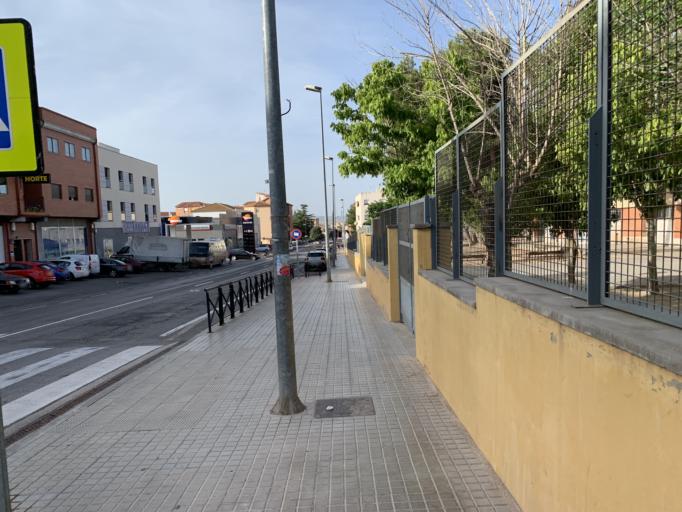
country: ES
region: Aragon
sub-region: Provincia de Teruel
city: Teruel
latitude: 40.3529
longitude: -1.1086
